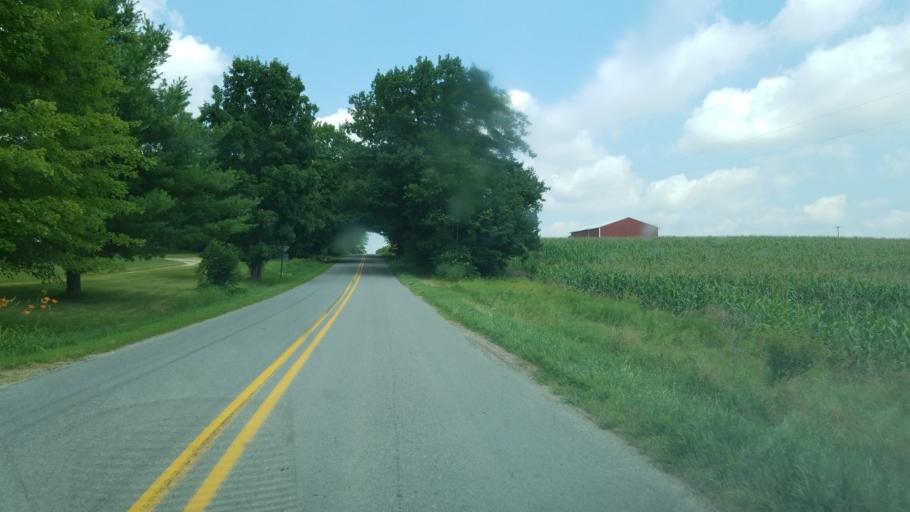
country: US
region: Michigan
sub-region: Kent County
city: Cedar Springs
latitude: 43.2797
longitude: -85.5114
